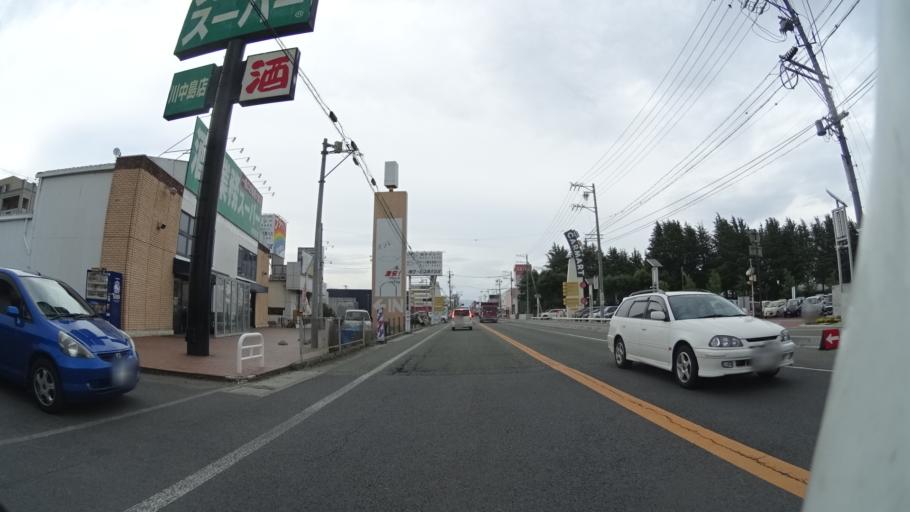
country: JP
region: Nagano
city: Nagano-shi
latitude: 36.5927
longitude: 138.1554
